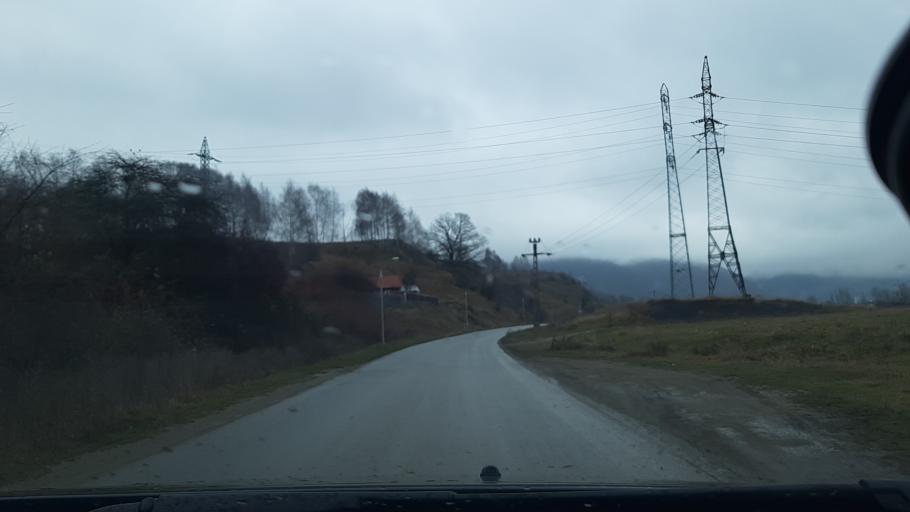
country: RO
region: Hunedoara
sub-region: Oras Petrila
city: Petrila
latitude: 45.4396
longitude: 23.4138
